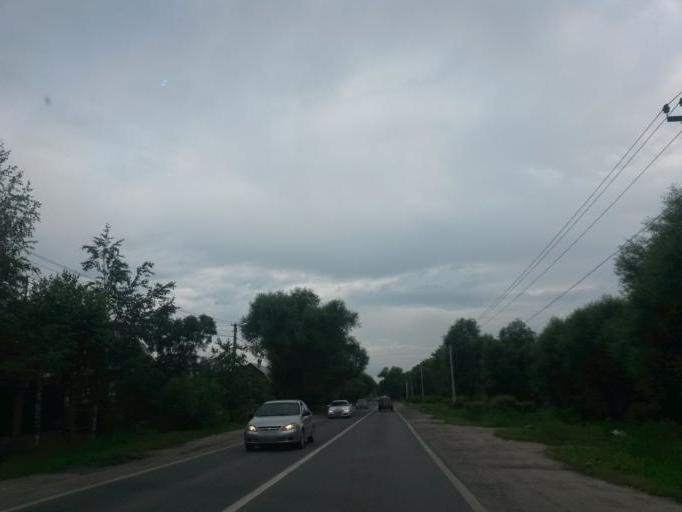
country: RU
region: Moskovskaya
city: Vostryakovo
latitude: 55.4005
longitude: 37.8139
